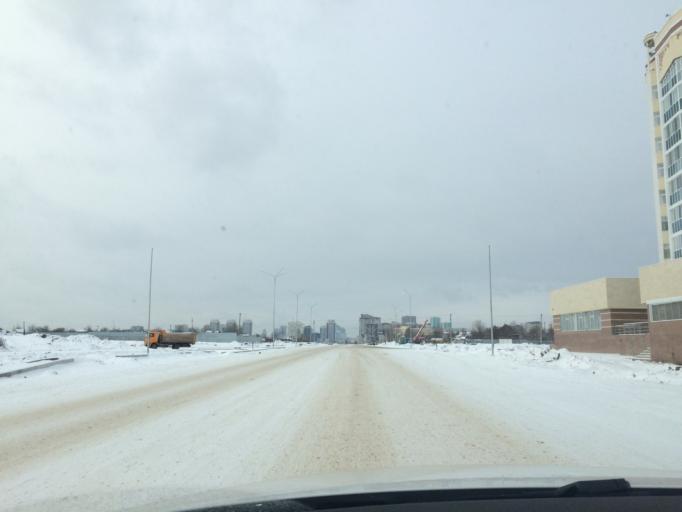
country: KZ
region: Astana Qalasy
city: Astana
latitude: 51.1191
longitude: 71.5048
